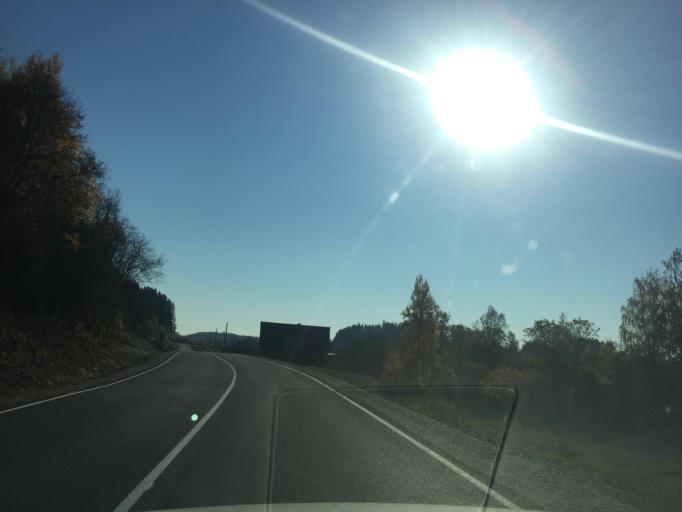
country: RU
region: Leningrad
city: Kuznechnoye
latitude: 61.3067
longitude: 29.8775
